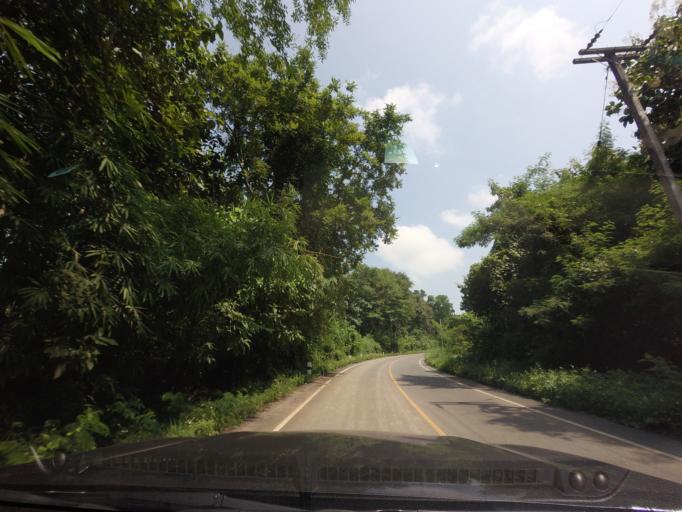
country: TH
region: Nan
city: Nan
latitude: 18.8462
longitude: 100.7776
